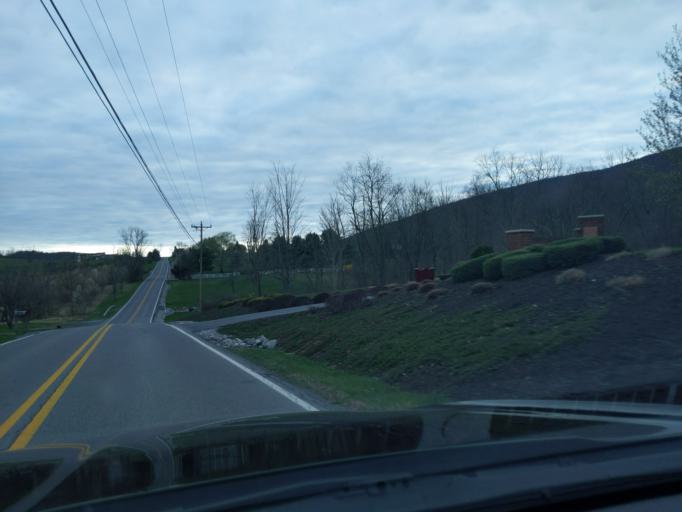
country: US
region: Pennsylvania
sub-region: Blair County
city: Greenwood
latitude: 40.4823
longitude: -78.3174
